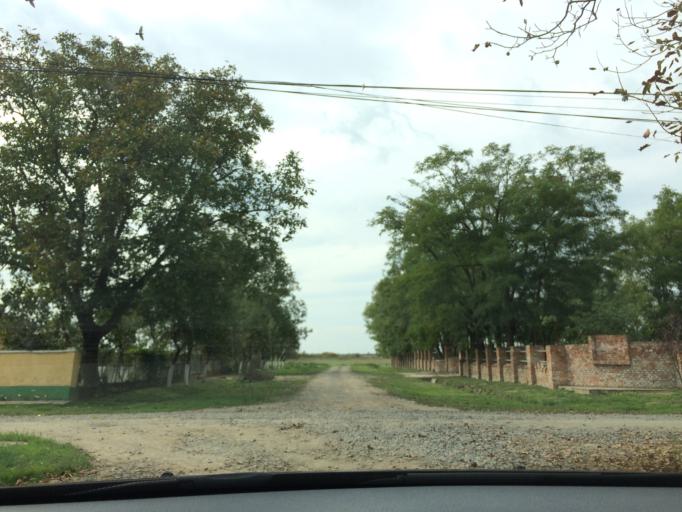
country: RO
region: Timis
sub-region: Comuna Cheveresu Mare
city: Cheveresu Mare
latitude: 45.7309
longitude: 21.4910
